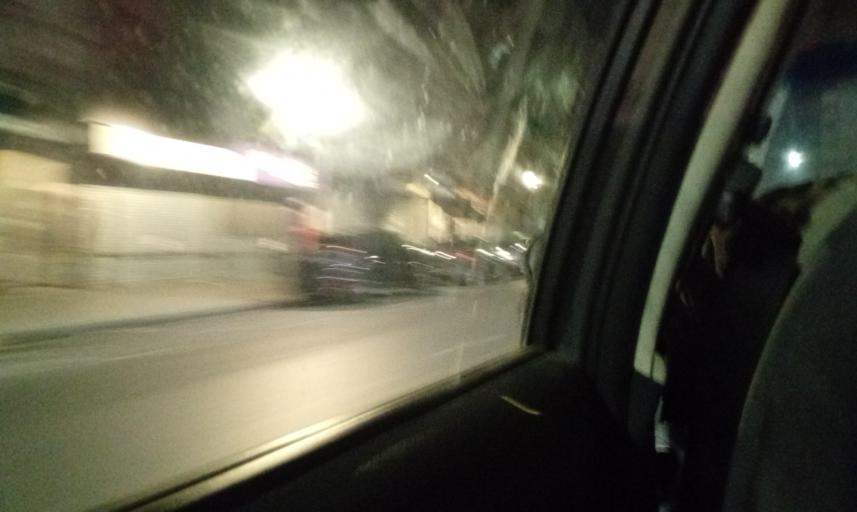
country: AR
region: Buenos Aires F.D.
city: Villa Santa Rita
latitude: -34.6268
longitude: -58.4730
